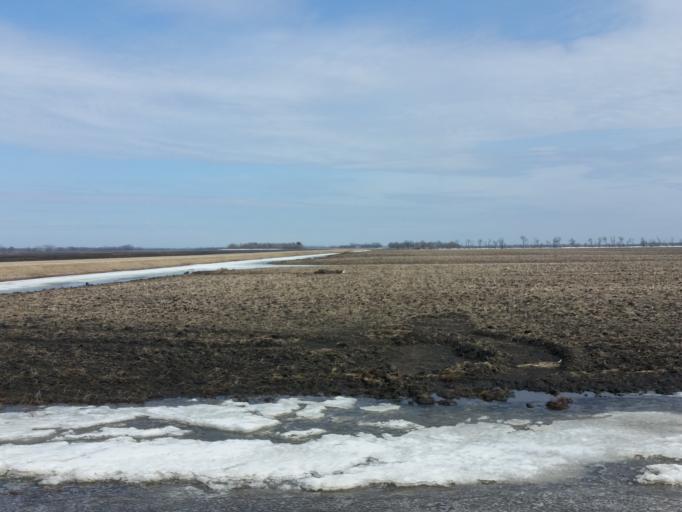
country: US
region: North Dakota
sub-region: Walsh County
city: Grafton
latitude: 48.4262
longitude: -97.2557
